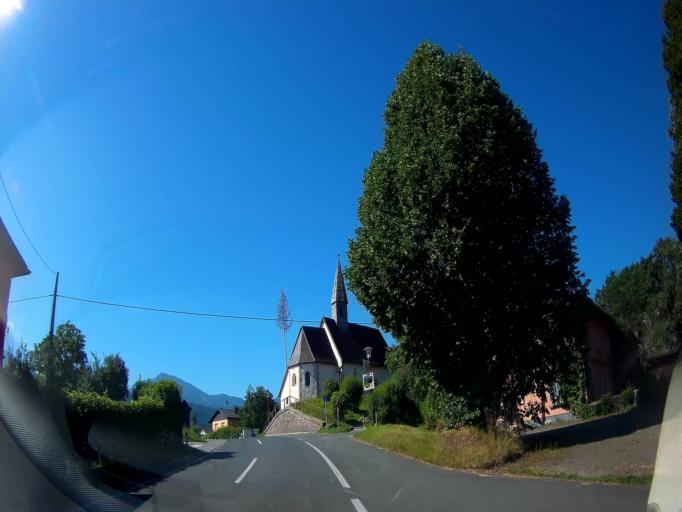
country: AT
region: Carinthia
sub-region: Politischer Bezirk Volkermarkt
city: Eberndorf
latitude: 46.5787
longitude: 14.6534
